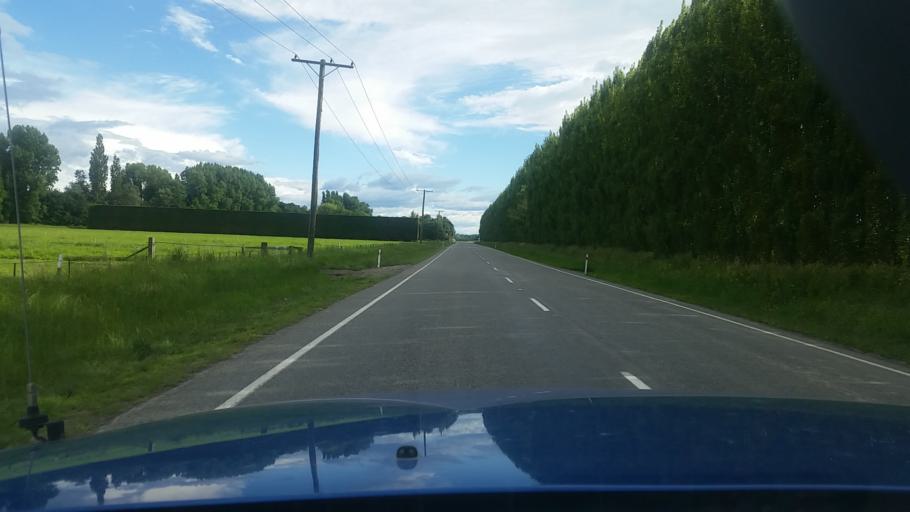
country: NZ
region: Canterbury
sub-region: Ashburton District
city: Ashburton
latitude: -43.8612
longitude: 171.7301
